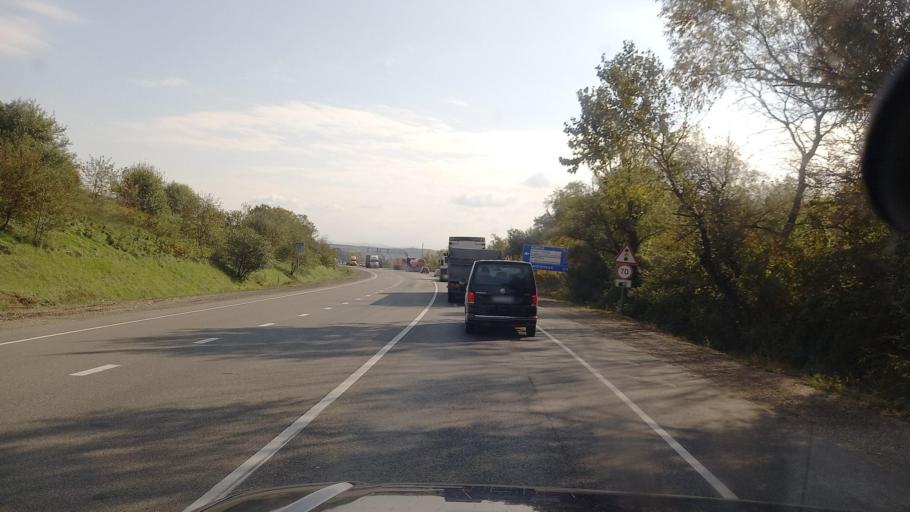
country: RU
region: Krasnodarskiy
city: Abinsk
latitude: 44.8490
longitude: 38.1386
